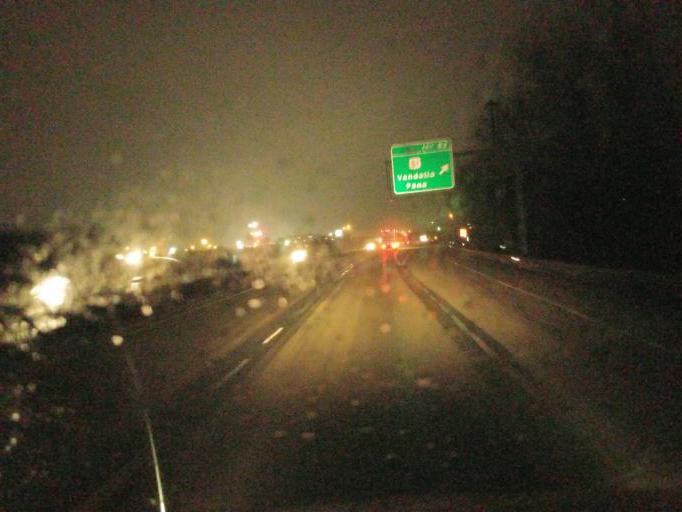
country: US
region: Illinois
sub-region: Fayette County
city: Vandalia
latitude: 38.9775
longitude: -89.0916
